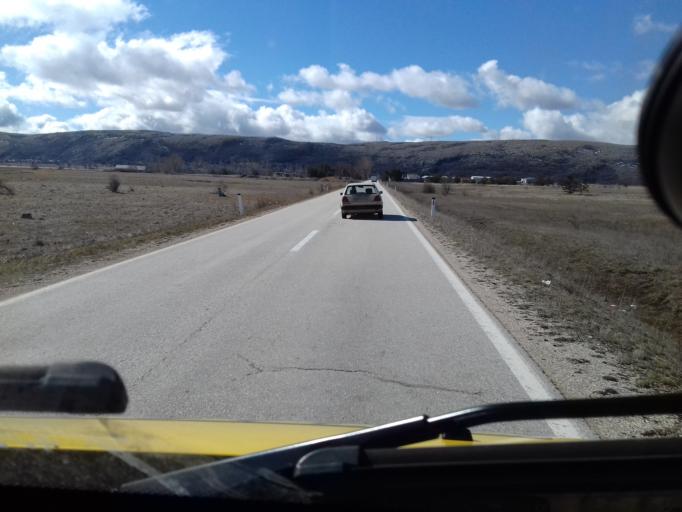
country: BA
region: Federation of Bosnia and Herzegovina
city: Tomislavgrad
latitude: 43.6890
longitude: 17.2080
